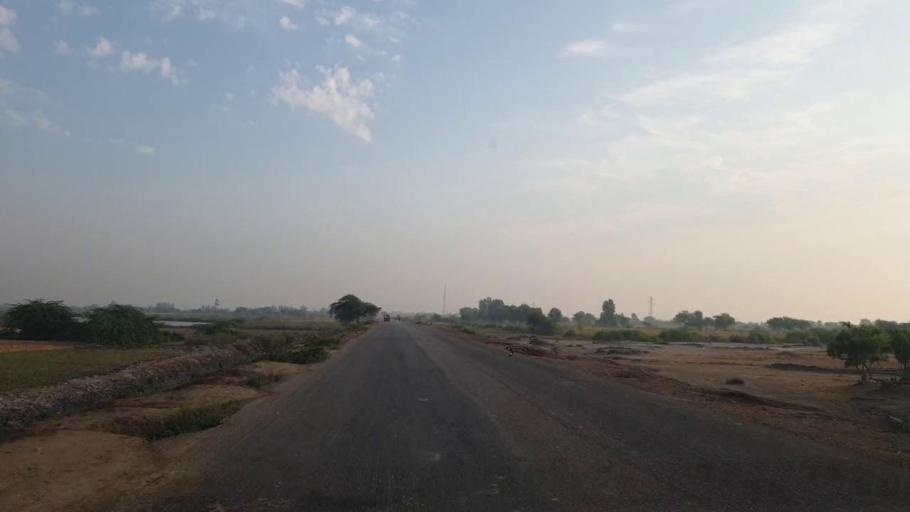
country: PK
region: Sindh
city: Badin
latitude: 24.7000
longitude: 68.9227
